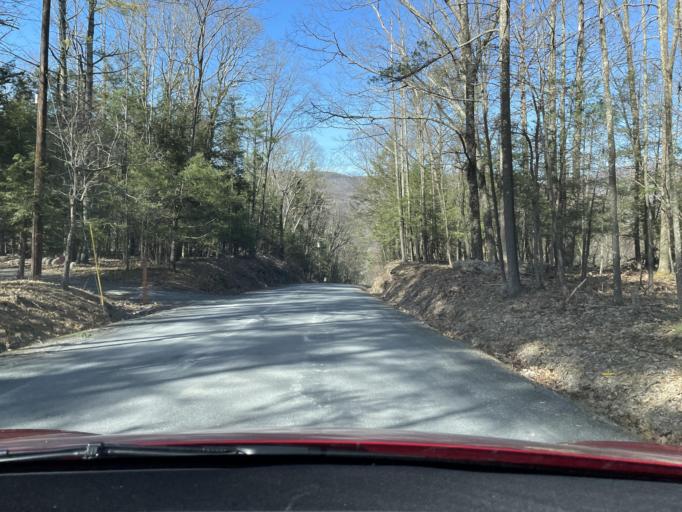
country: US
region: New York
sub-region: Ulster County
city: Woodstock
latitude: 42.0279
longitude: -74.1473
